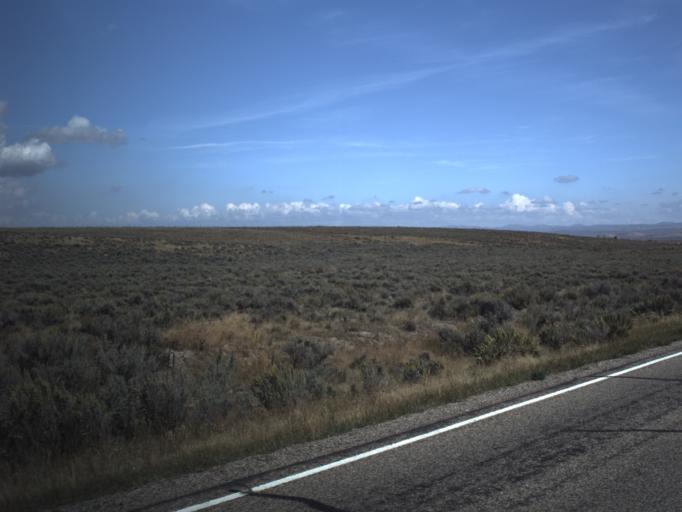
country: US
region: Utah
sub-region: Rich County
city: Randolph
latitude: 41.7715
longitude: -111.1328
